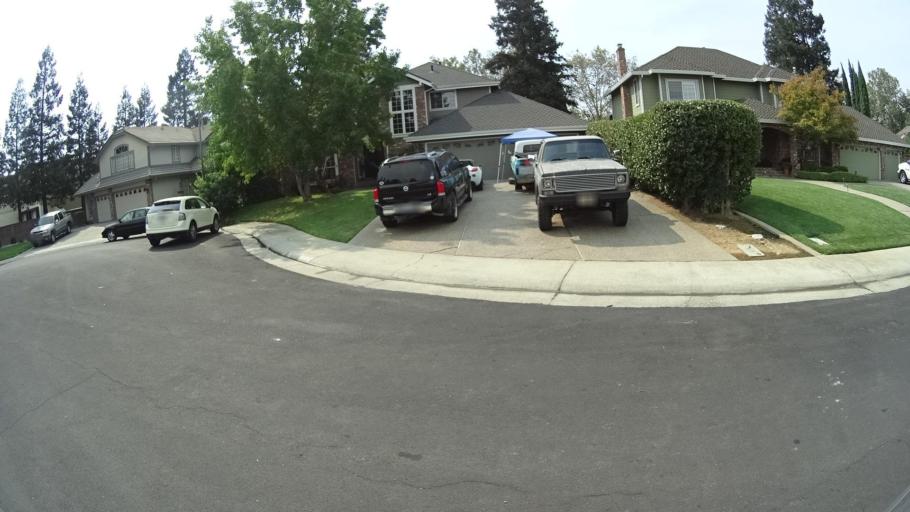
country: US
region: California
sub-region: Sacramento County
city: Elk Grove
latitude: 38.4251
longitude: -121.3741
